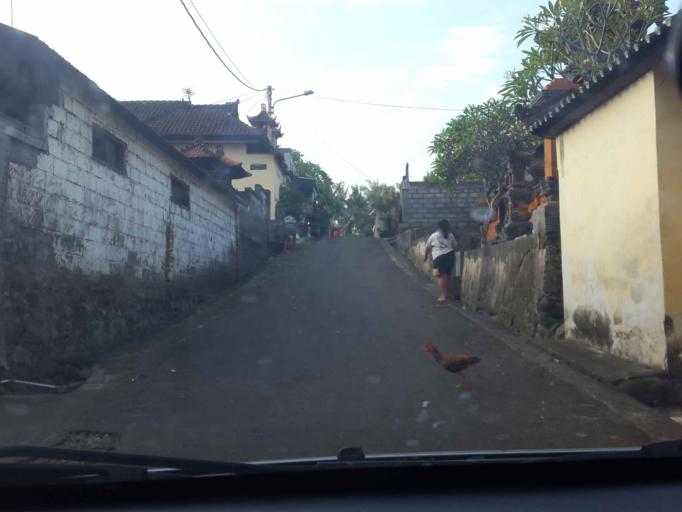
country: ID
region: Bali
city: Semarapura
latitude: -8.5333
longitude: 115.4129
